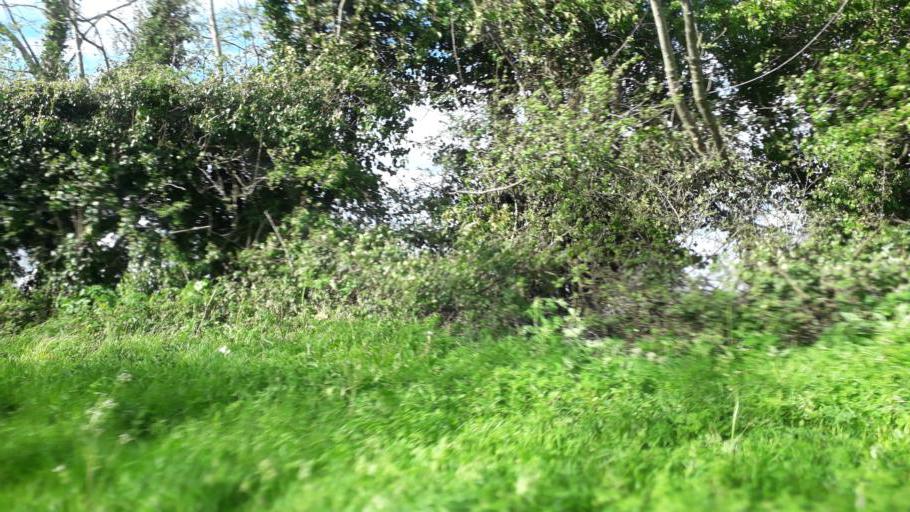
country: IE
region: Leinster
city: Ballymun
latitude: 53.4473
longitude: -6.2705
